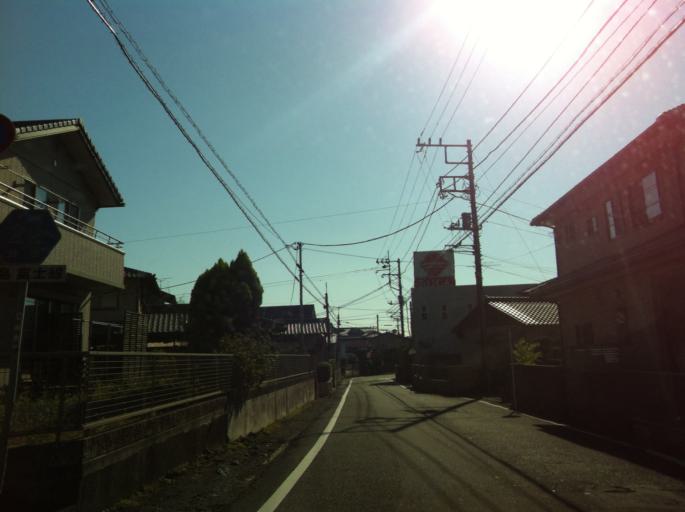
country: JP
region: Shizuoka
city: Fuji
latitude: 35.1621
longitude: 138.7445
